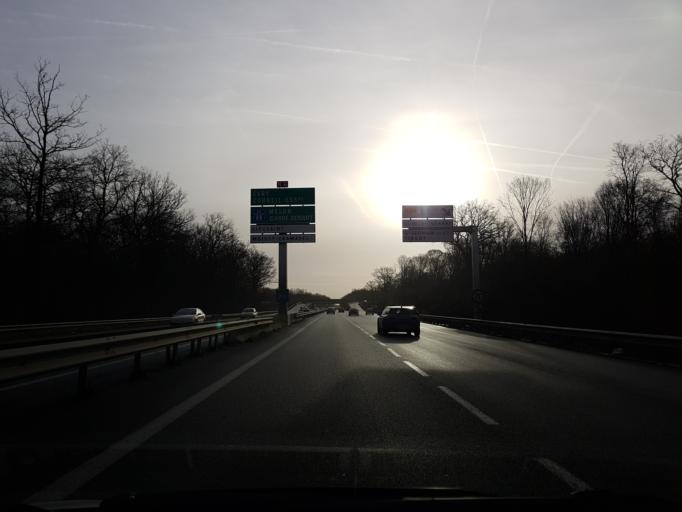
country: FR
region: Ile-de-France
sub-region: Departement de l'Essonne
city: Tigery
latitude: 48.6636
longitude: 2.5141
